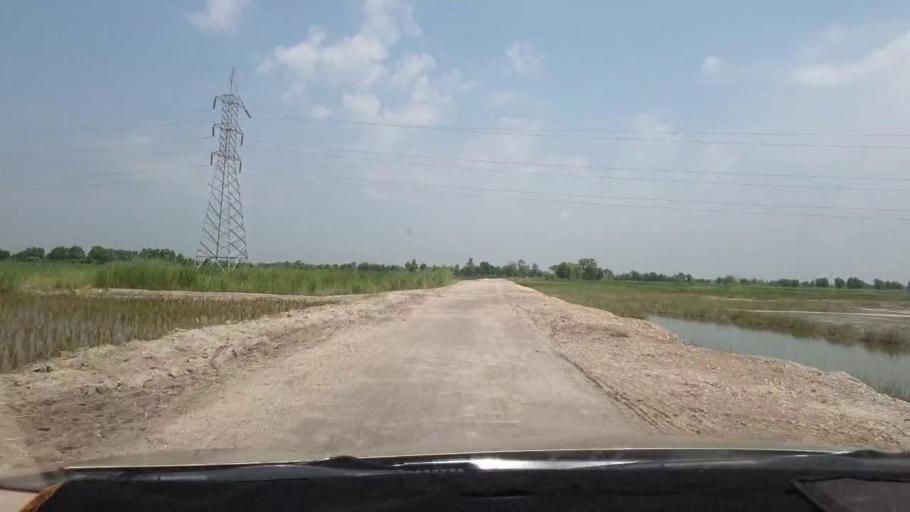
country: PK
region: Sindh
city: Naudero
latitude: 27.7347
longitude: 68.3413
